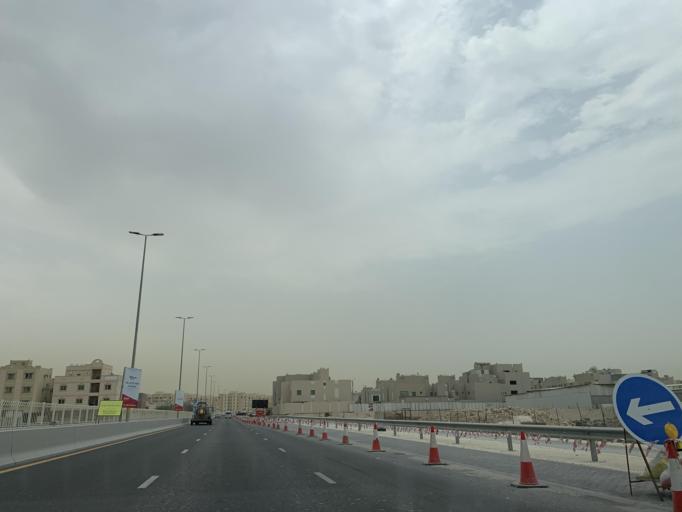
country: BH
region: Northern
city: Madinat `Isa
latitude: 26.1809
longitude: 50.5204
